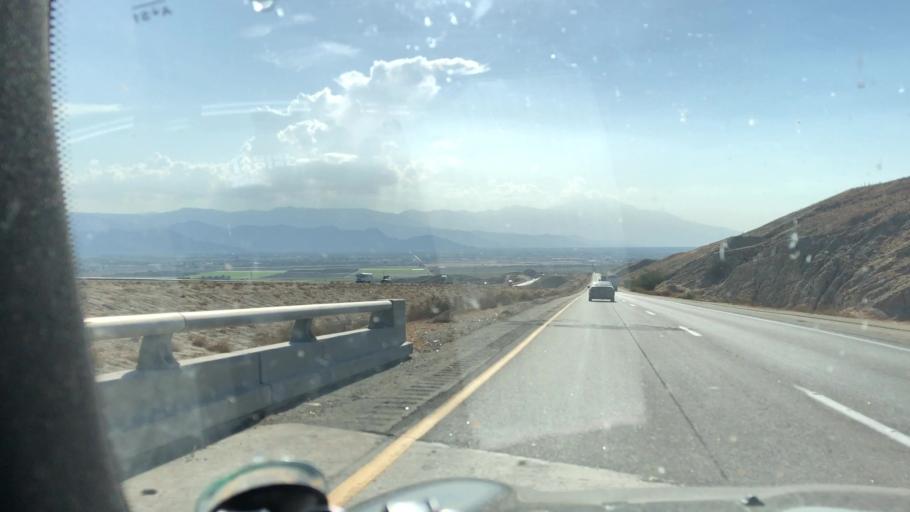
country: US
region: California
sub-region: Riverside County
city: Thermal
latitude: 33.6991
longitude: -116.1058
